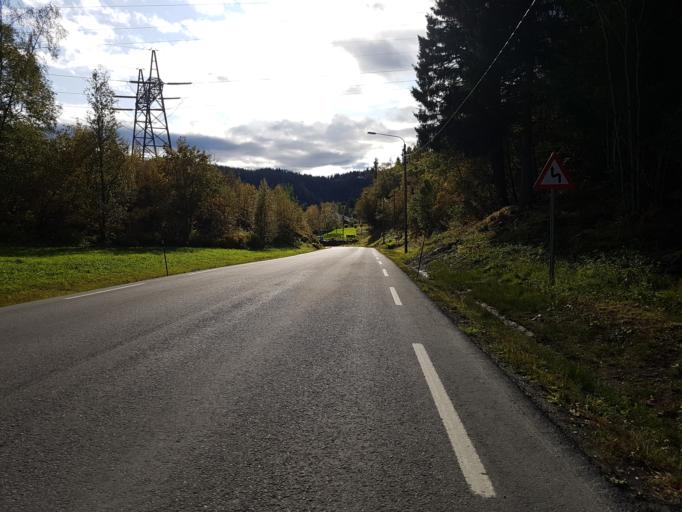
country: NO
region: Sor-Trondelag
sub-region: Klaebu
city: Klaebu
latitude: 63.4011
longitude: 10.5240
